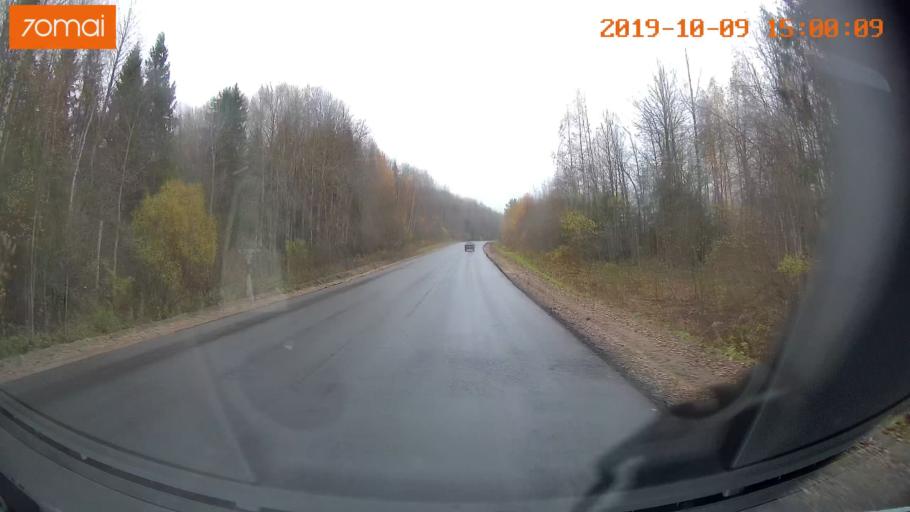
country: RU
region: Kostroma
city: Chistyye Bory
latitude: 58.3125
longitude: 41.6759
